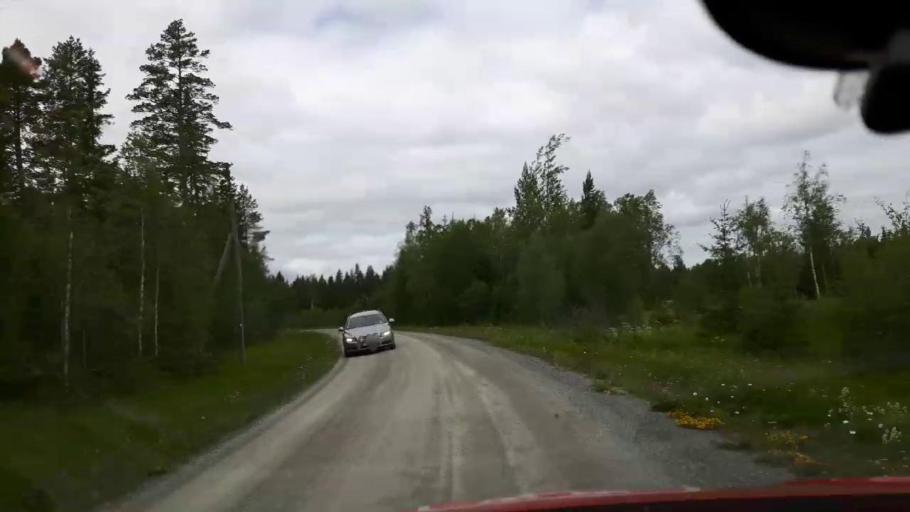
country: SE
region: Jaemtland
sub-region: OEstersunds Kommun
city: Brunflo
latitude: 63.0609
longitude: 14.9112
